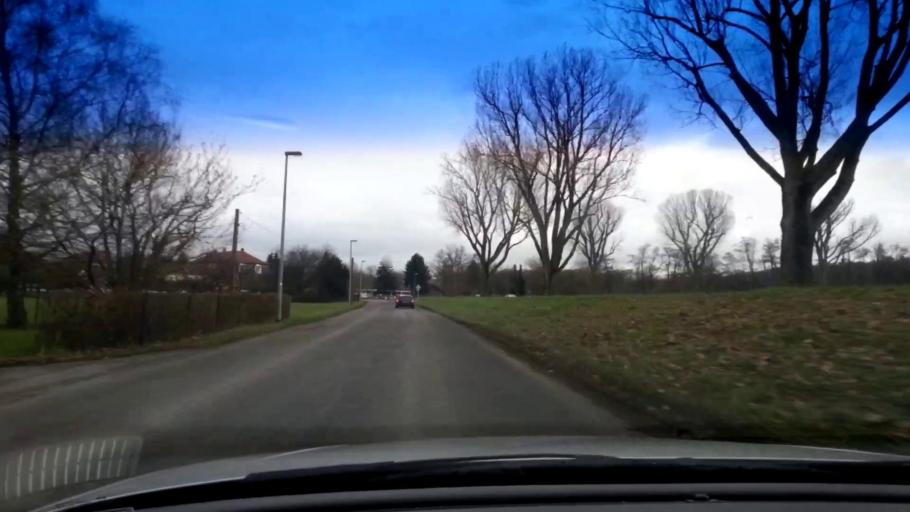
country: DE
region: Bavaria
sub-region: Upper Franconia
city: Bamberg
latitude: 49.8704
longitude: 10.9089
